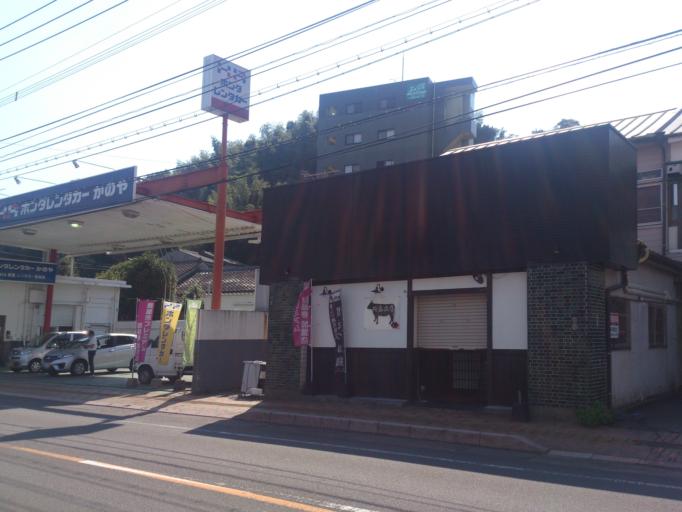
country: JP
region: Kagoshima
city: Kanoya
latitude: 31.3873
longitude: 130.8499
